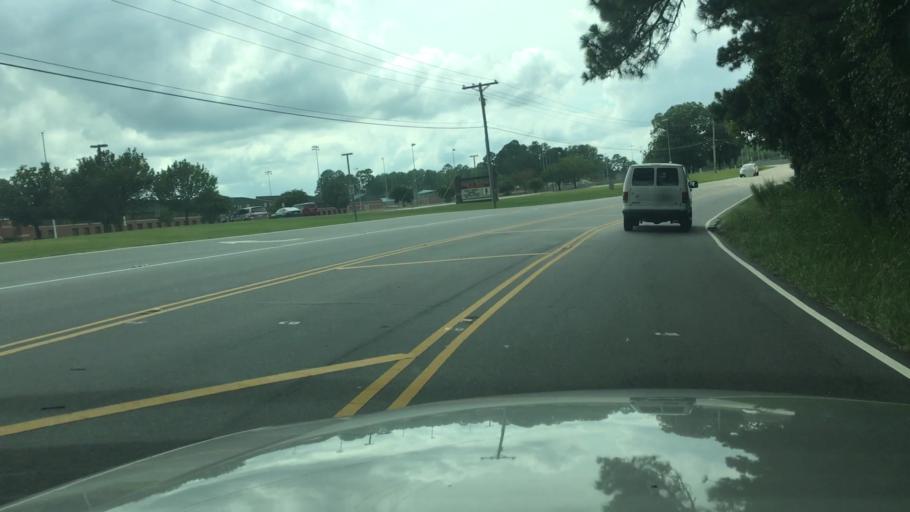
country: US
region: North Carolina
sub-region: Cumberland County
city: Hope Mills
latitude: 35.0012
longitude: -78.9876
